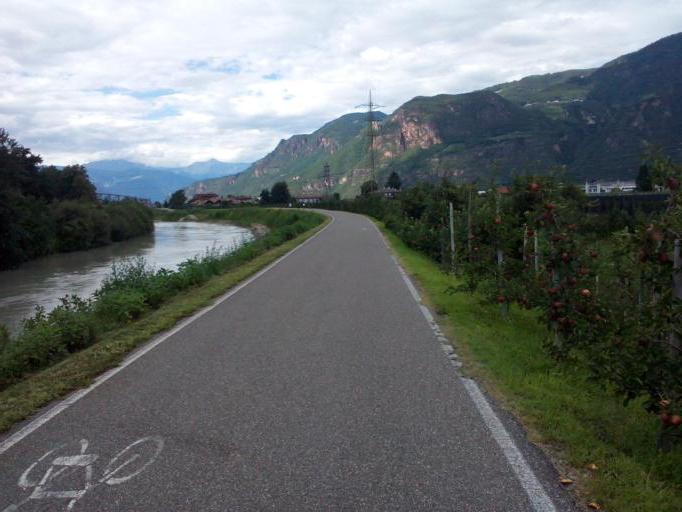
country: IT
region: Trentino-Alto Adige
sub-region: Bolzano
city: Cornaiano
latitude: 46.4806
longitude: 11.3077
